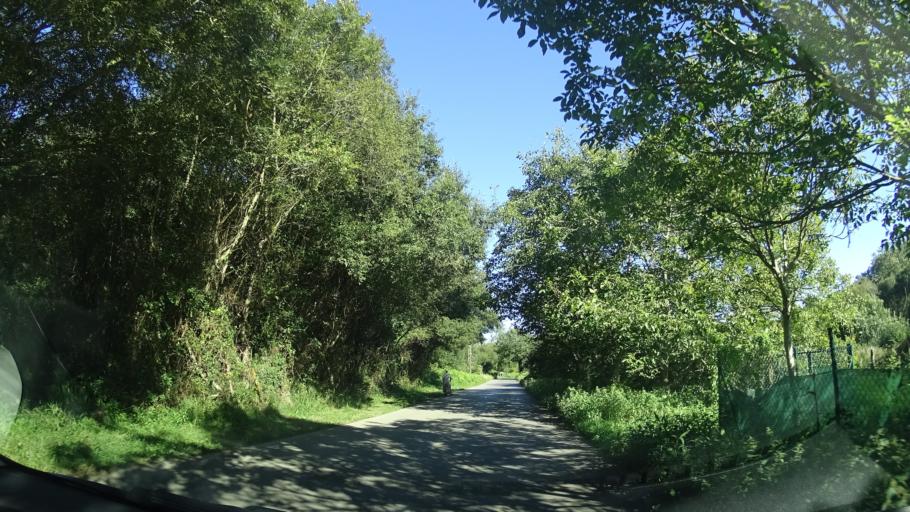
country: ES
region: Asturias
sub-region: Province of Asturias
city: Ribadesella
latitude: 43.4741
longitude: -5.1327
